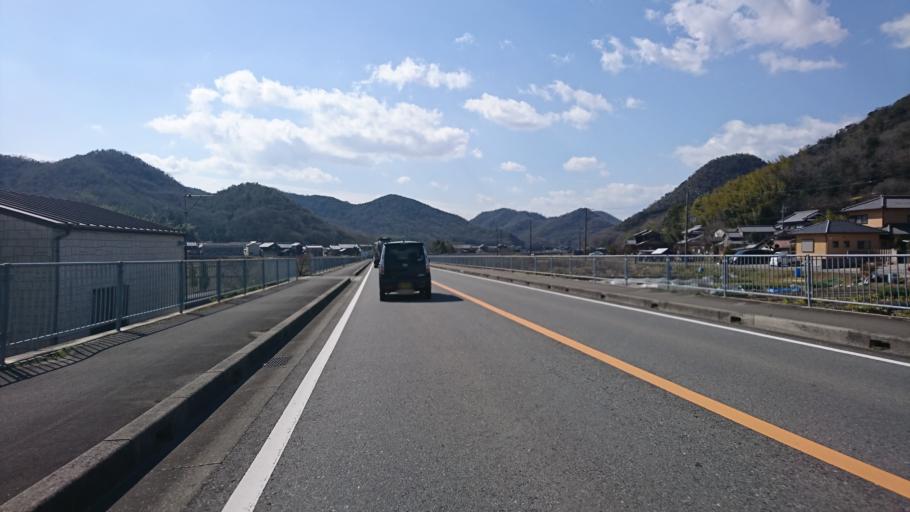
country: JP
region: Hyogo
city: Kakogawacho-honmachi
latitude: 34.8619
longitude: 134.7902
